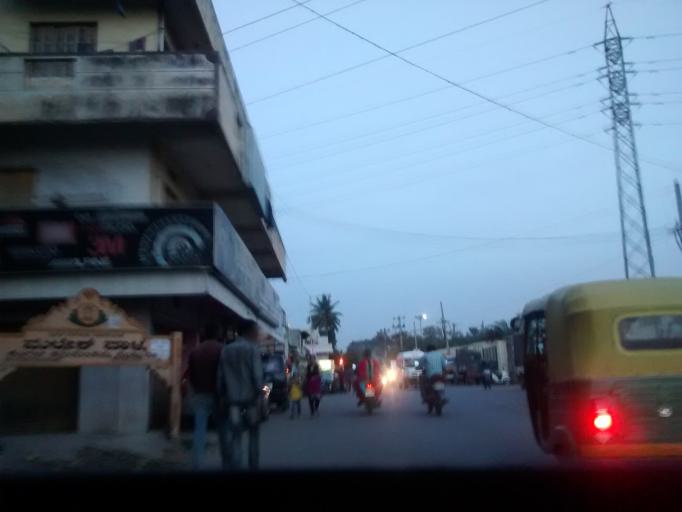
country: IN
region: Karnataka
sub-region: Bangalore Urban
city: Bangalore
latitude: 12.9753
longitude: 77.6691
